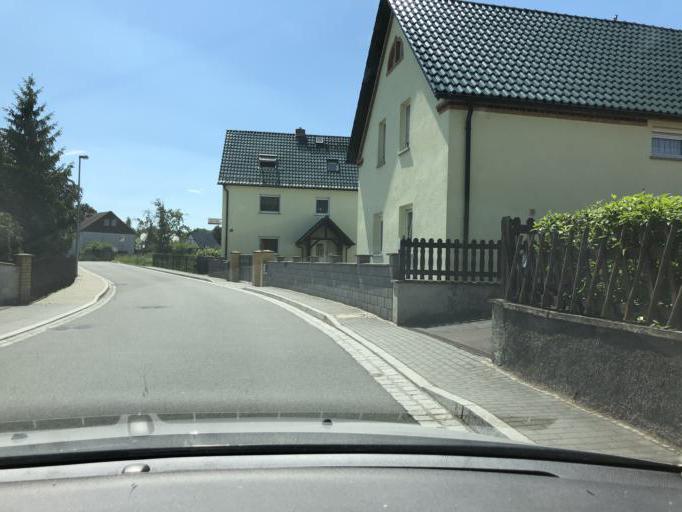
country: DE
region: Saxony
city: Grimma
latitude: 51.2902
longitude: 12.6890
